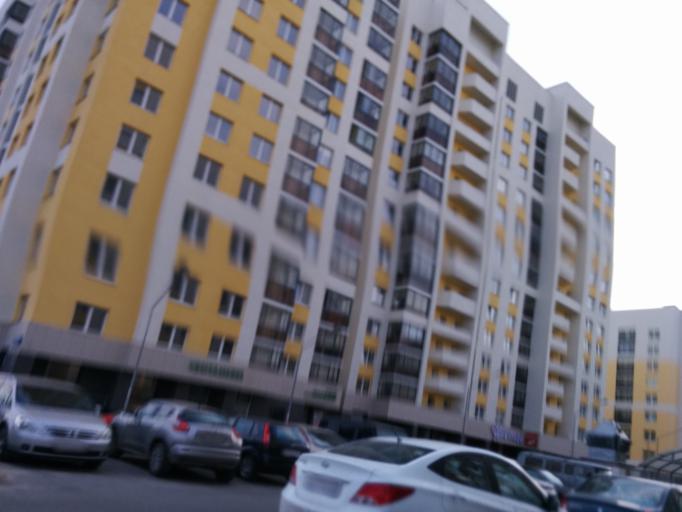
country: RU
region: Sverdlovsk
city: Sovkhoznyy
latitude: 56.7877
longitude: 60.5282
